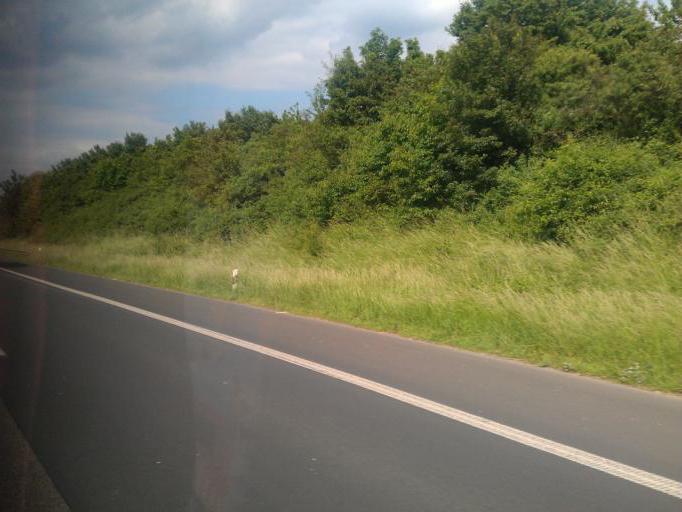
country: DE
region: North Rhine-Westphalia
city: Wesseling
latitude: 50.8526
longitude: 6.9685
